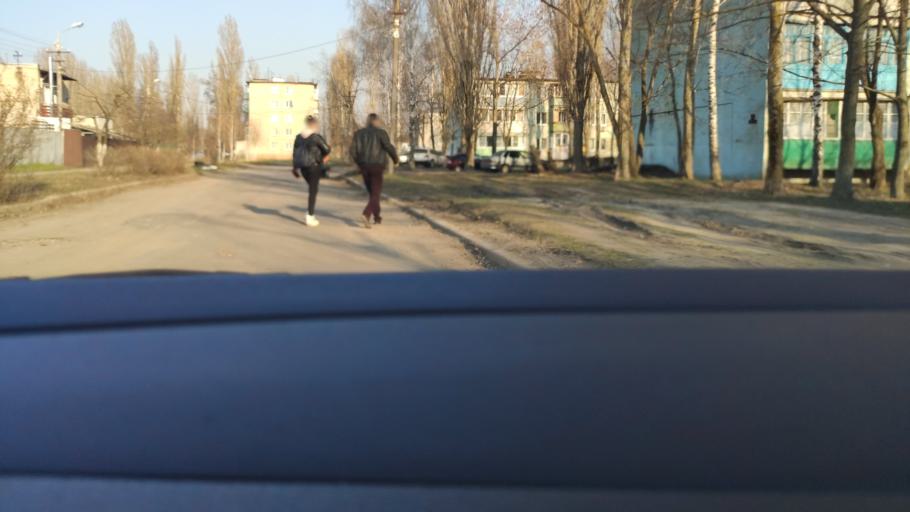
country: RU
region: Voronezj
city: Maslovka
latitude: 51.5864
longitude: 39.3174
